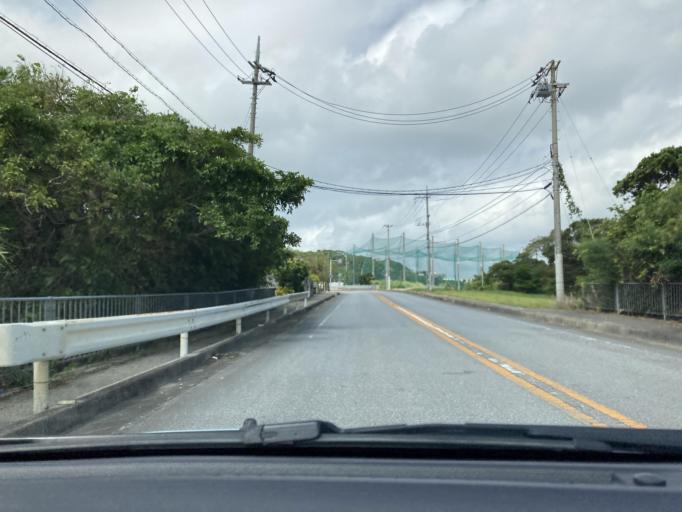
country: JP
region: Okinawa
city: Ishikawa
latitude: 26.4083
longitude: 127.8366
